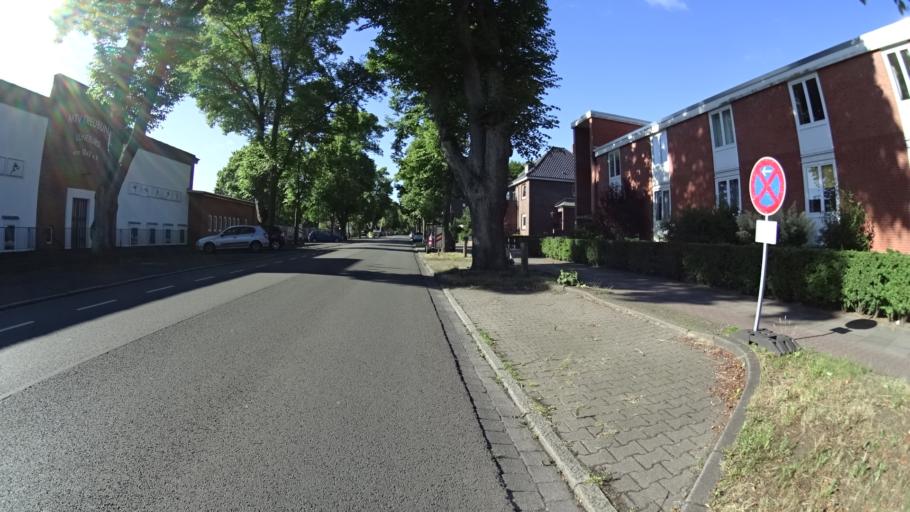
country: DE
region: Lower Saxony
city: Lueneburg
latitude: 53.2342
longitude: 10.4049
